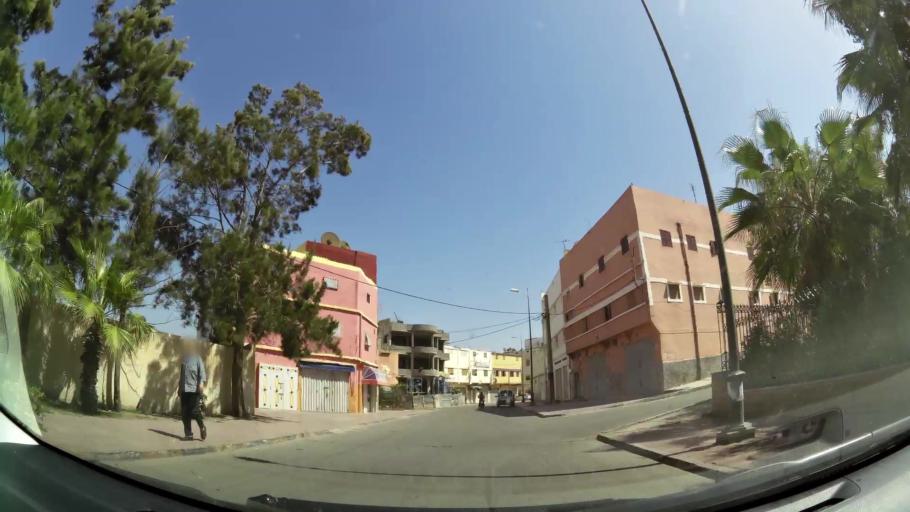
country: MA
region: Souss-Massa-Draa
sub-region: Inezgane-Ait Mellou
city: Inezgane
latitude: 30.3516
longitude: -9.5357
